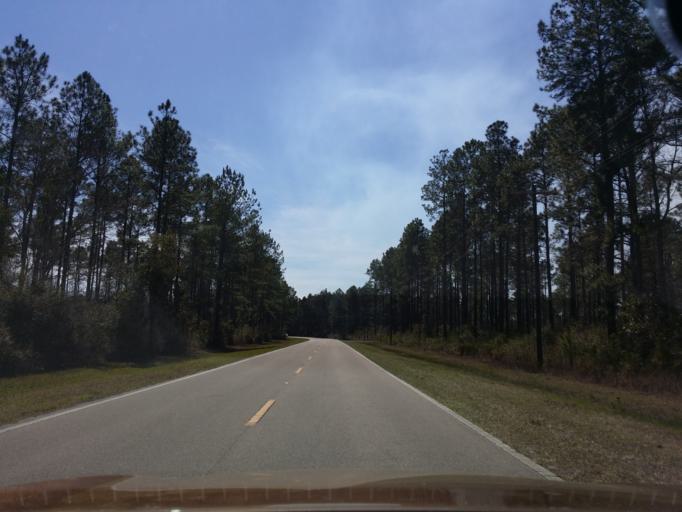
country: US
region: Florida
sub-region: Leon County
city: Woodville
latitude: 30.3233
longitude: -84.1503
